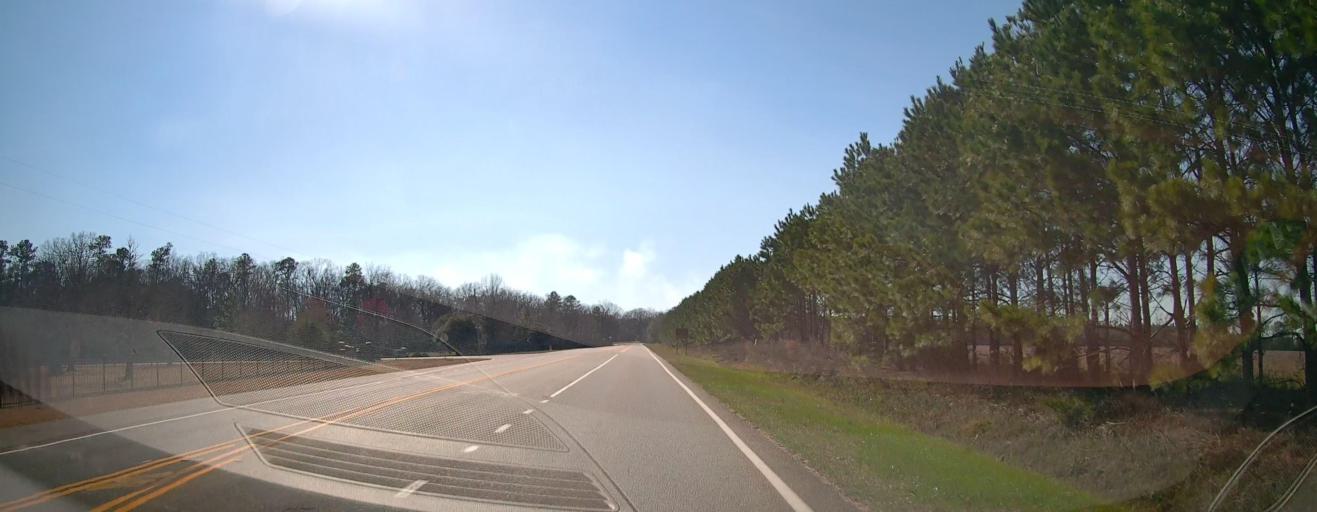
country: US
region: Georgia
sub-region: Macon County
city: Oglethorpe
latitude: 32.2075
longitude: -84.1279
